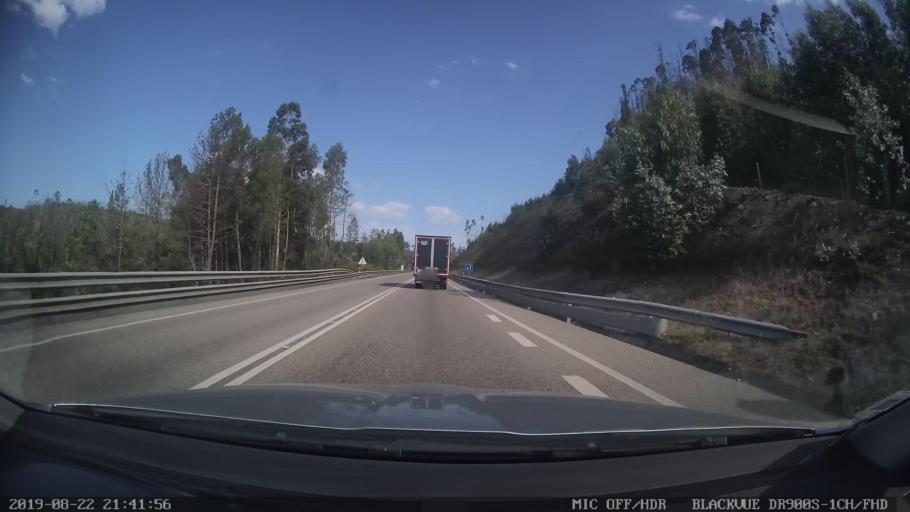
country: PT
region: Leiria
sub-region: Figueiro Dos Vinhos
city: Figueiro dos Vinhos
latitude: 39.9283
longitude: -8.3335
